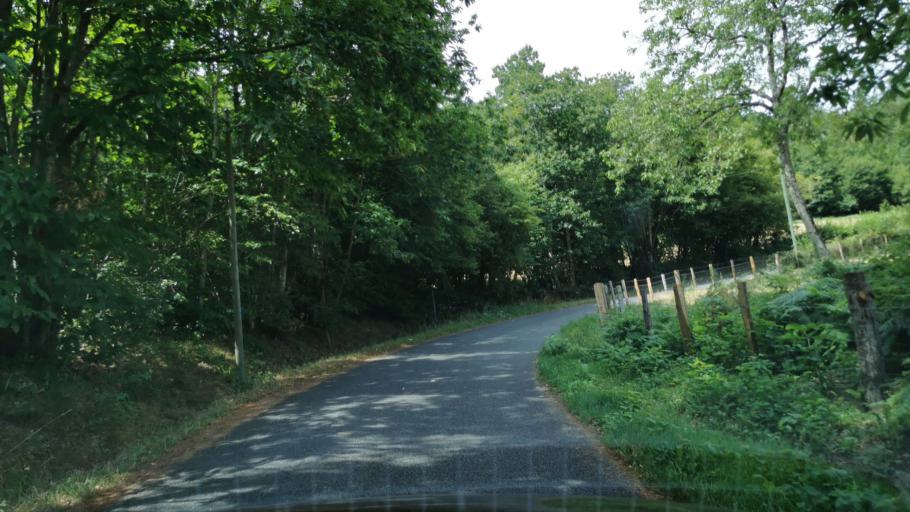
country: FR
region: Bourgogne
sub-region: Departement de Saone-et-Loire
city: Marmagne
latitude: 46.8053
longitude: 4.3061
